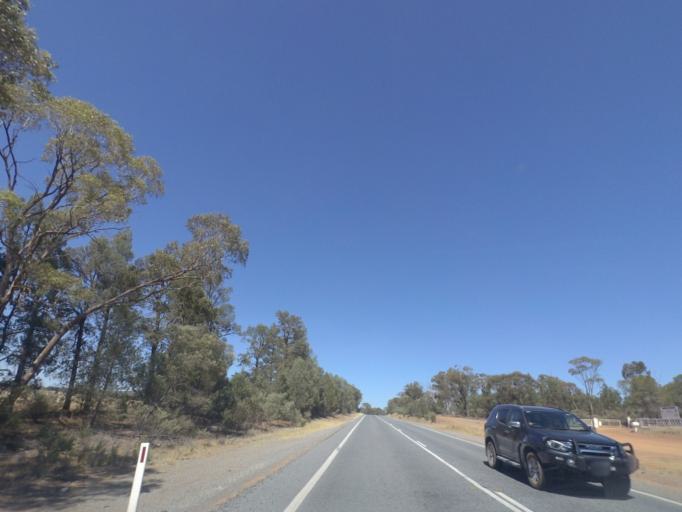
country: AU
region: New South Wales
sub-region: Narrandera
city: Narrandera
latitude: -34.4179
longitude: 146.8523
